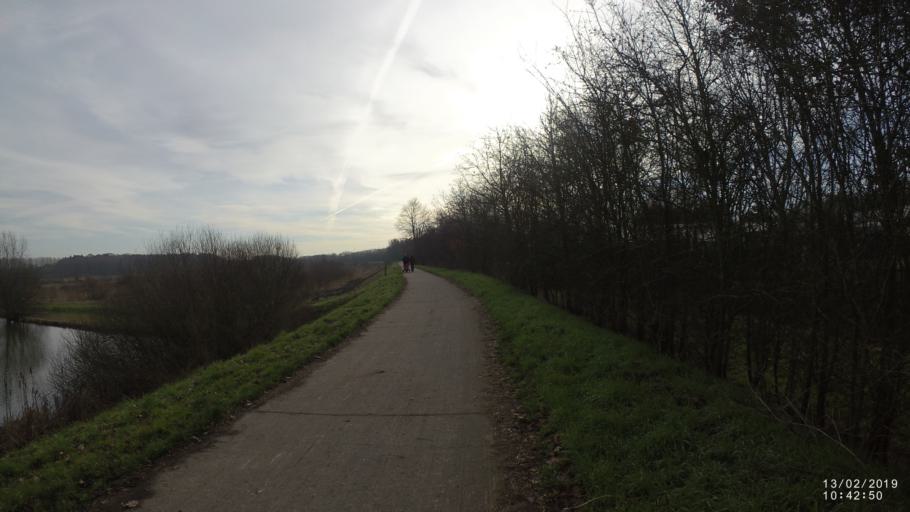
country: BE
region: Flanders
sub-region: Provincie Vlaams-Brabant
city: Diest
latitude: 50.9682
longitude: 5.0773
